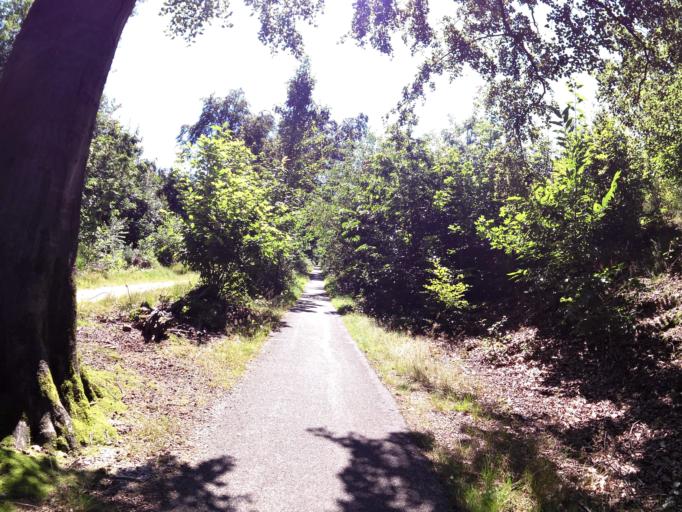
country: NL
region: Gelderland
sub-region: Gemeente Groesbeek
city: Berg en Dal
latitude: 51.7890
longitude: 5.8873
